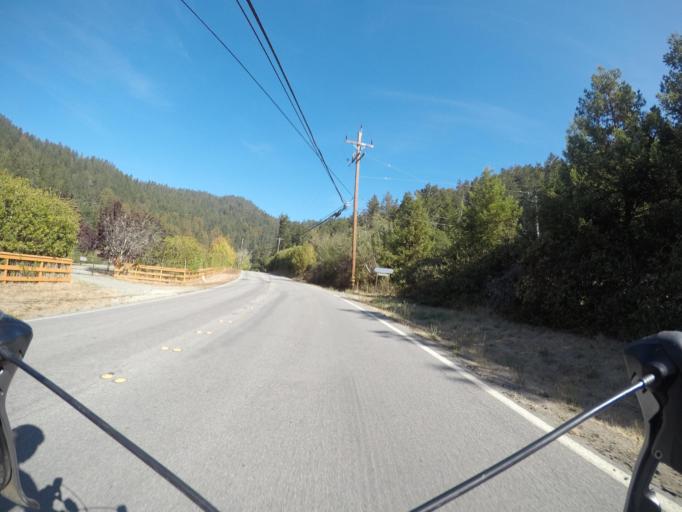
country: US
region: California
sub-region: San Mateo County
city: Portola Valley
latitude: 37.2638
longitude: -122.3217
